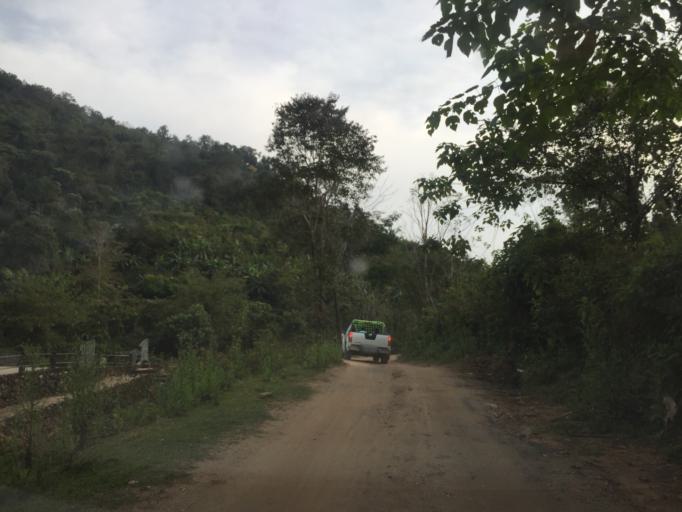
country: TH
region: Chiang Mai
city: Samoeng
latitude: 19.0107
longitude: 98.7313
